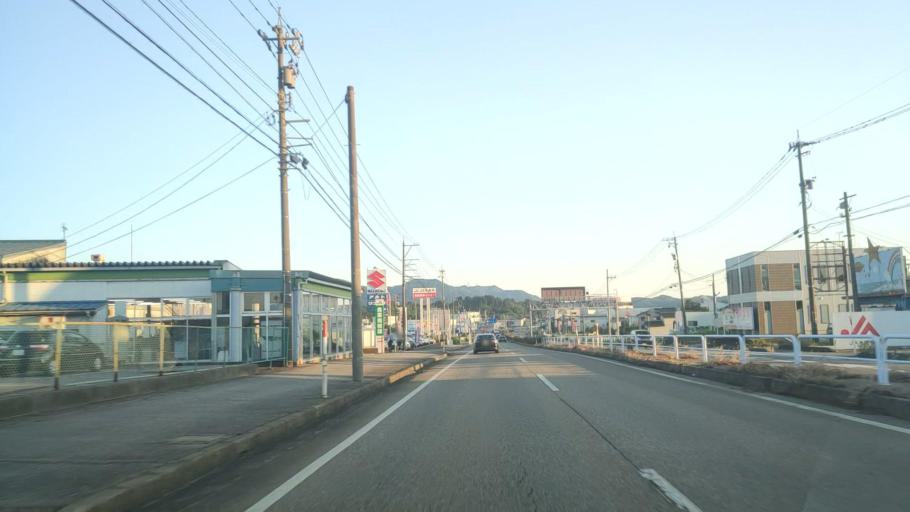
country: JP
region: Toyama
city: Himi
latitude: 36.8277
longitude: 136.9934
